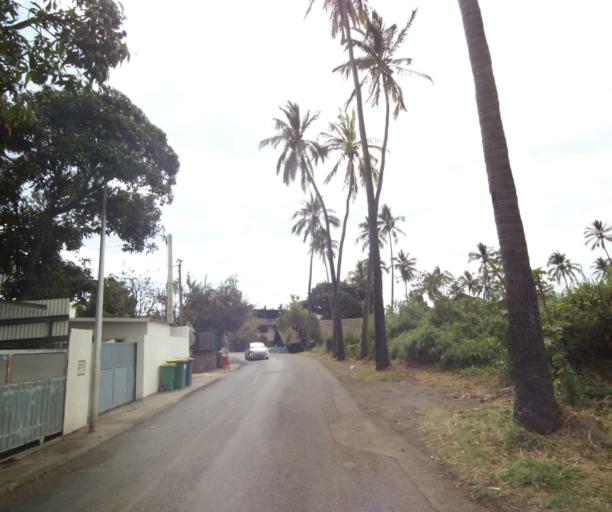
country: RE
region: Reunion
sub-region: Reunion
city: Saint-Paul
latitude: -21.0120
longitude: 55.2773
